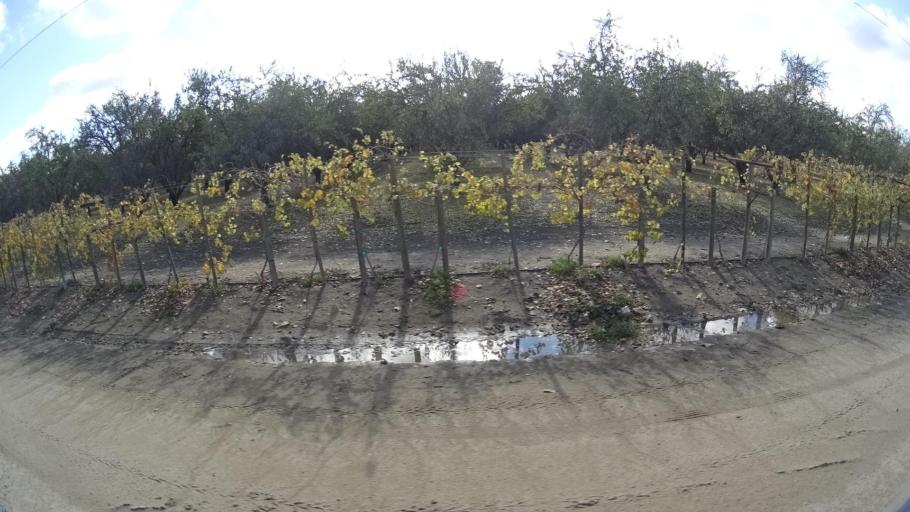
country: US
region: California
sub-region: Kern County
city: McFarland
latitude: 35.6888
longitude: -119.2420
